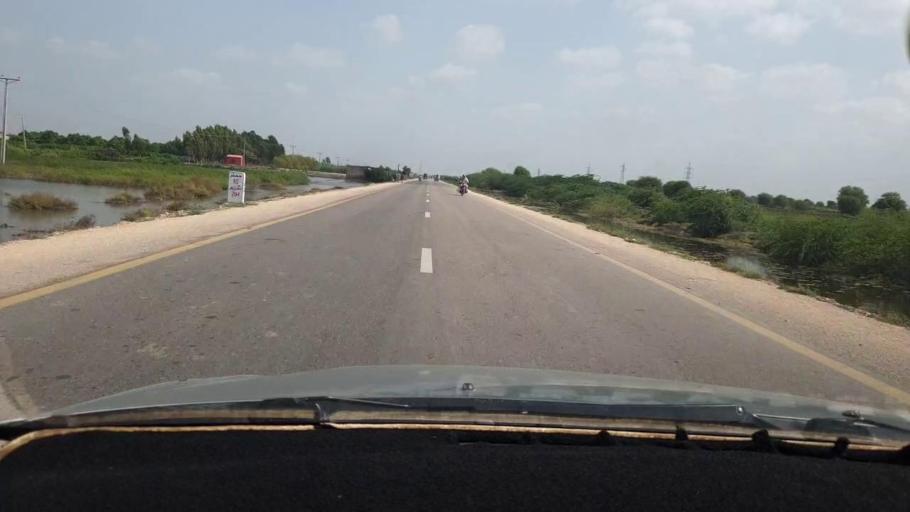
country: PK
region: Sindh
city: Digri
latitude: 25.0425
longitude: 69.2325
